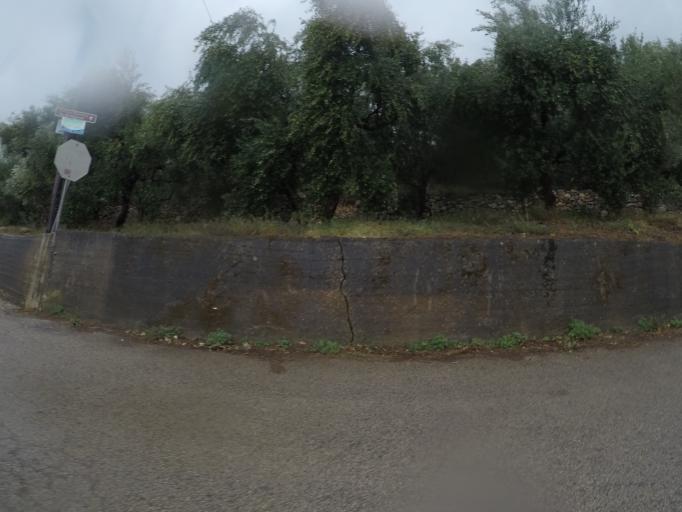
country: GR
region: Peloponnese
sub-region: Nomos Messinias
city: Kyparissia
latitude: 37.2512
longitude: 21.6875
